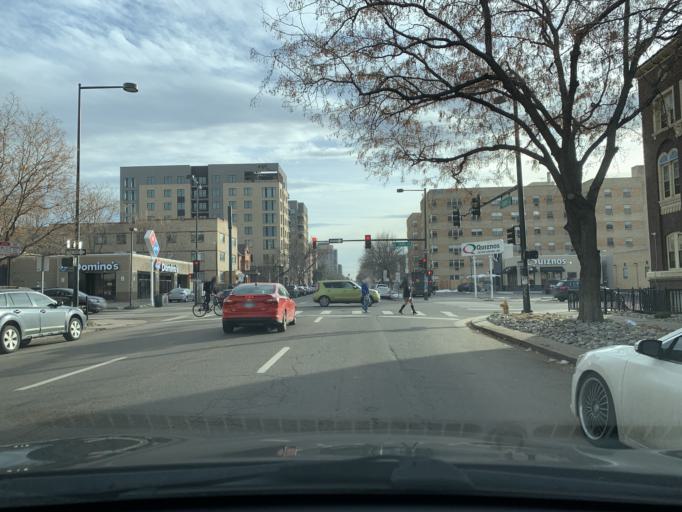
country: US
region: Colorado
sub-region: Denver County
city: Denver
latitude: 39.7372
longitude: -104.9836
